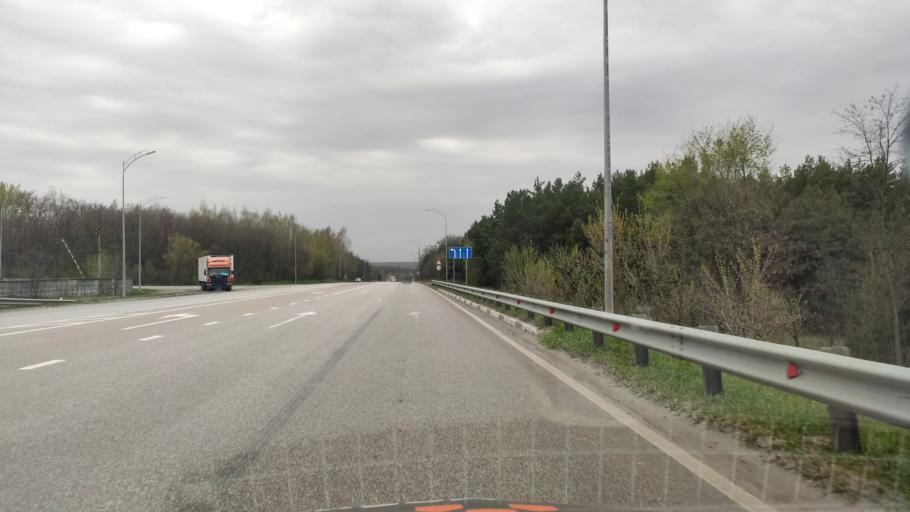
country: RU
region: Belgorod
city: Staryy Oskol
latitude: 51.3614
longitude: 37.8372
